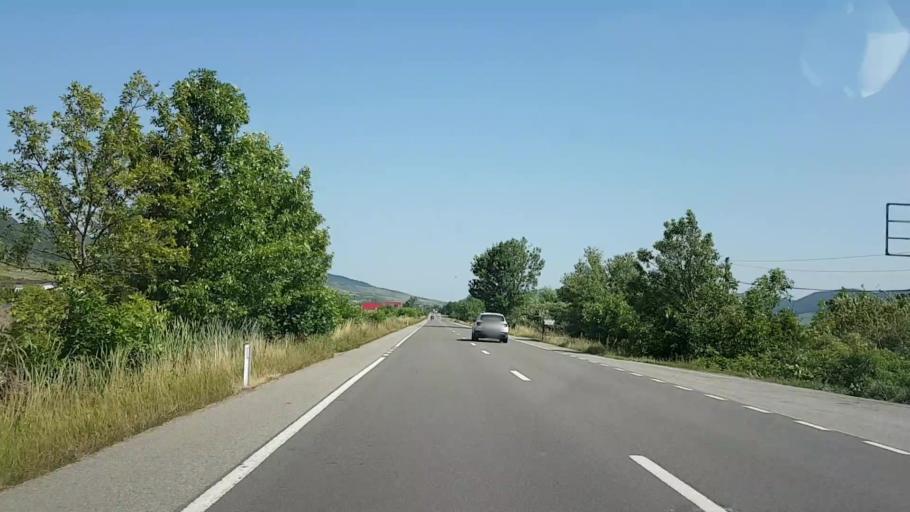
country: RO
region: Bistrita-Nasaud
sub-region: Comuna Sieu-Magherus
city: Sieu-Magherus
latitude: 47.1040
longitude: 24.3552
